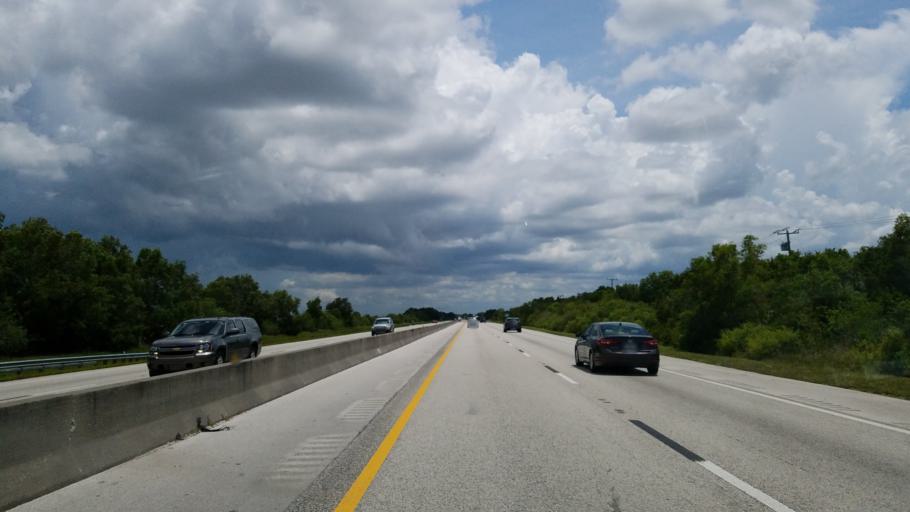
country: US
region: Florida
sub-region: Saint Lucie County
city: White City
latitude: 27.3671
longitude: -80.3805
